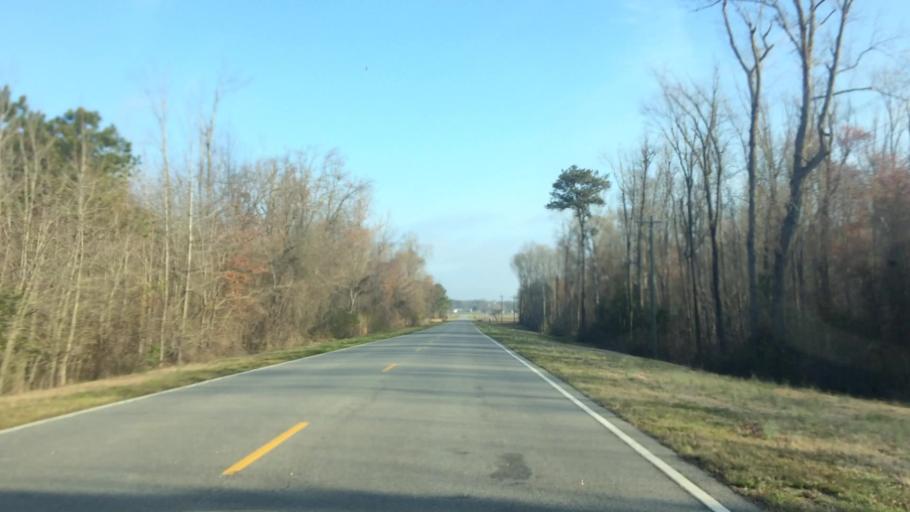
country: US
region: North Carolina
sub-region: Edgecombe County
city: Pinetops
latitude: 35.7184
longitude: -77.6340
